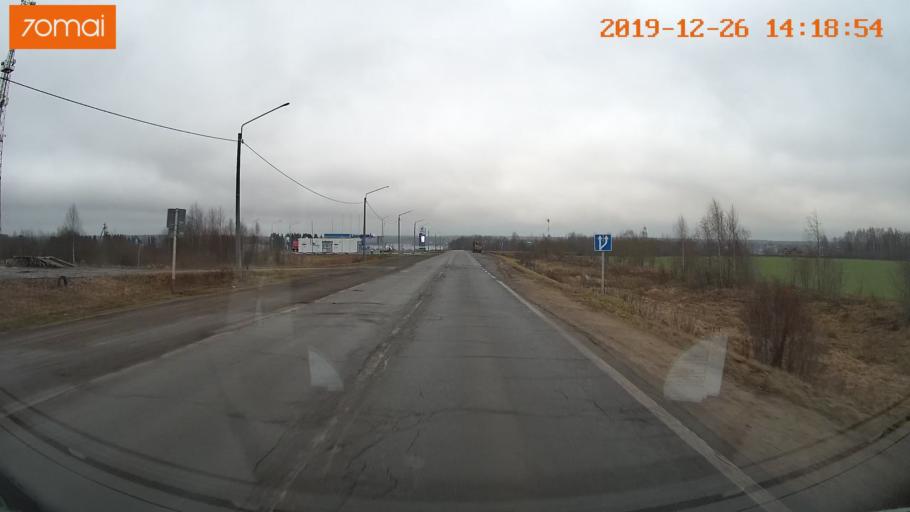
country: RU
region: Jaroslavl
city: Poshekhon'ye
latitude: 58.5129
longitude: 39.1057
